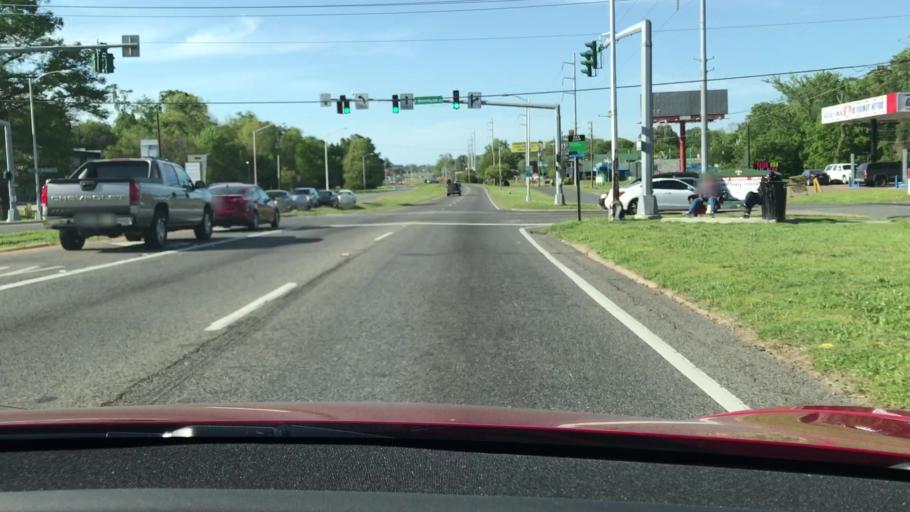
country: US
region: Louisiana
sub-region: Bossier Parish
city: Bossier City
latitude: 32.4845
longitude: -93.7240
